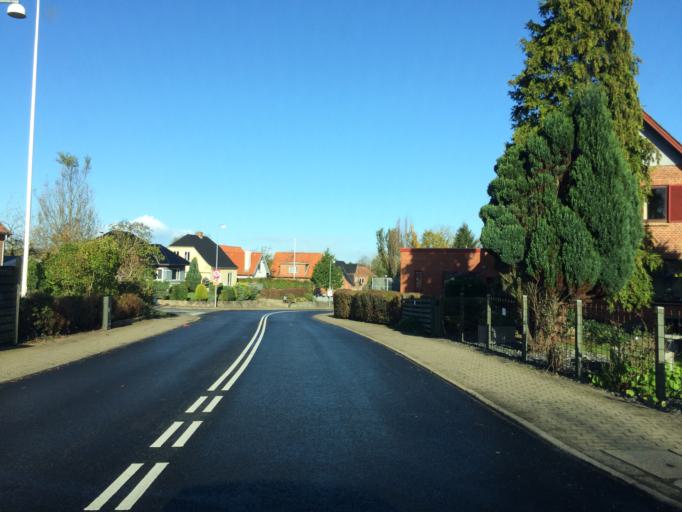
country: DK
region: South Denmark
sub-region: Fredericia Kommune
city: Taulov
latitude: 55.5430
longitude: 9.6129
